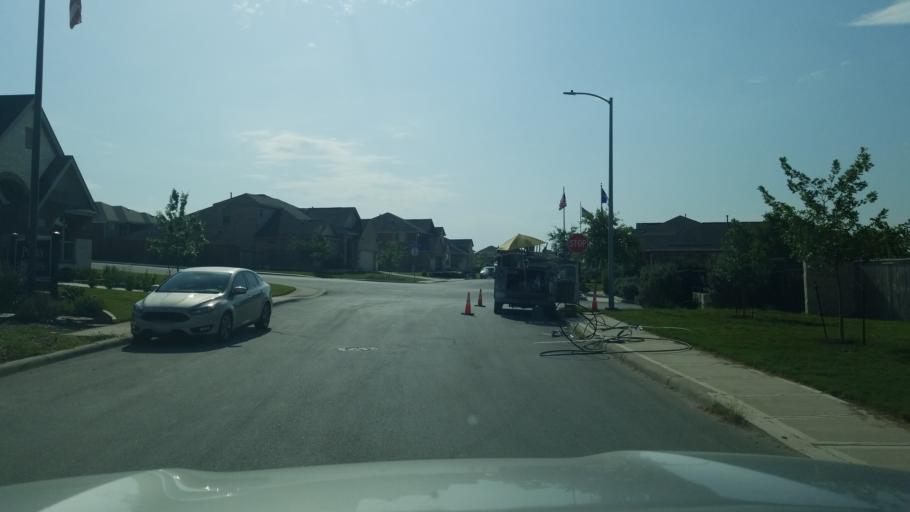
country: US
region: Texas
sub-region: Medina County
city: La Coste
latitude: 29.4022
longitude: -98.7852
